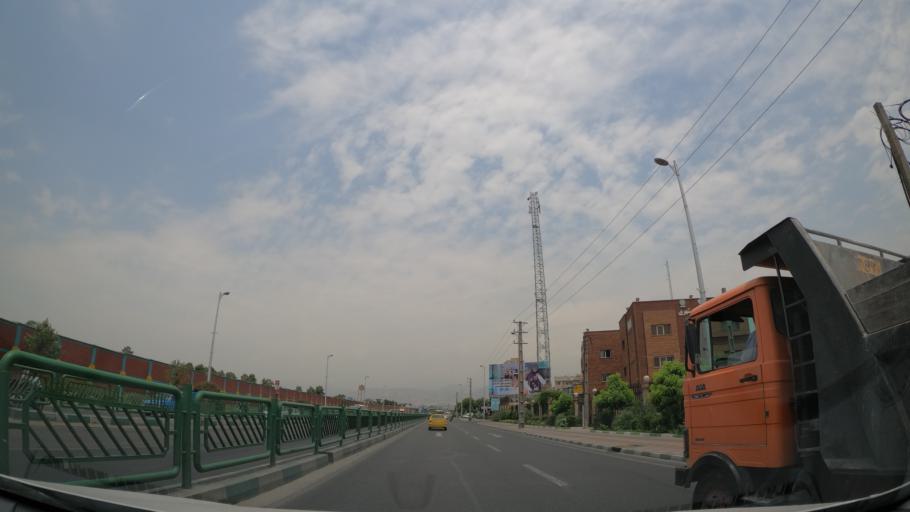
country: IR
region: Tehran
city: Tehran
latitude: 35.6863
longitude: 51.3415
